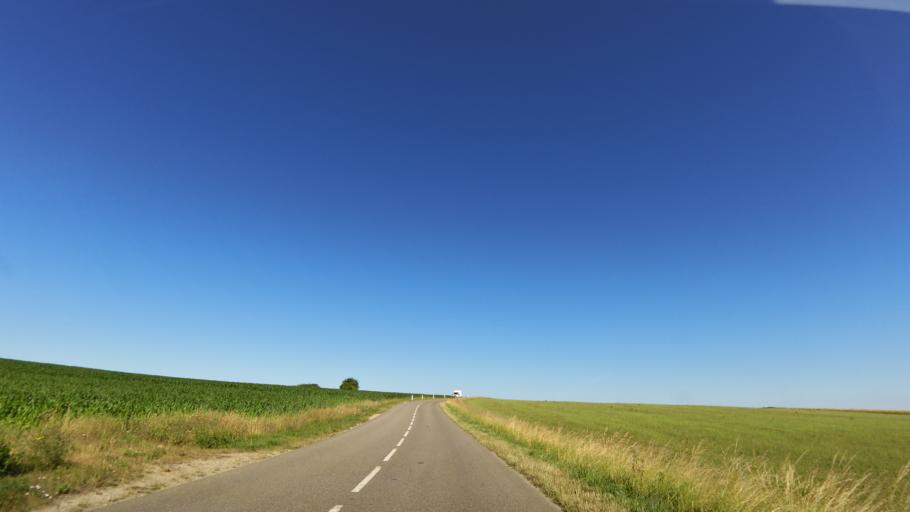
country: FR
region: Lorraine
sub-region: Departement de la Moselle
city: Lorquin
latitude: 48.6363
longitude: 6.9538
